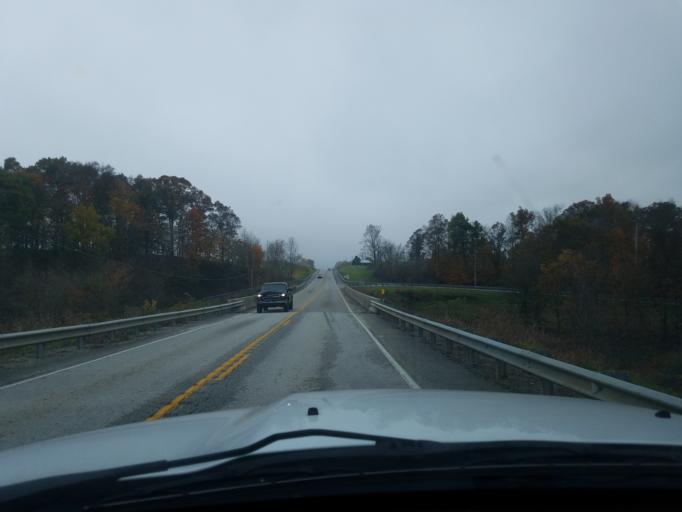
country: US
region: Kentucky
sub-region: Taylor County
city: Campbellsville
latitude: 37.3695
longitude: -85.4033
